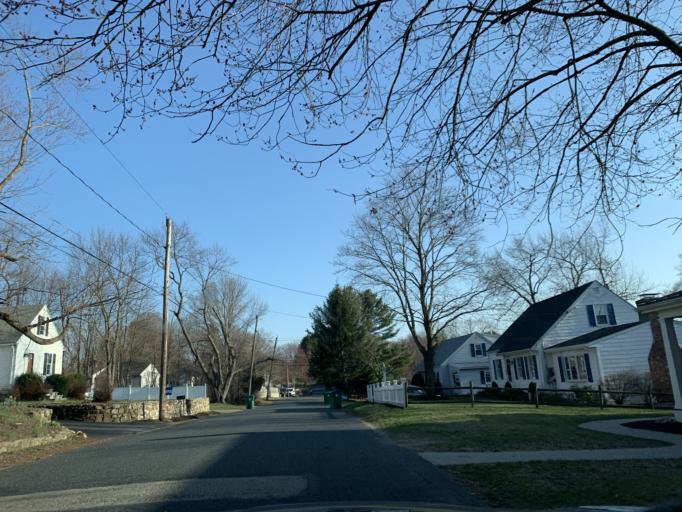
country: US
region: Massachusetts
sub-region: Norfolk County
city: Dedham
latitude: 42.2238
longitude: -71.1779
